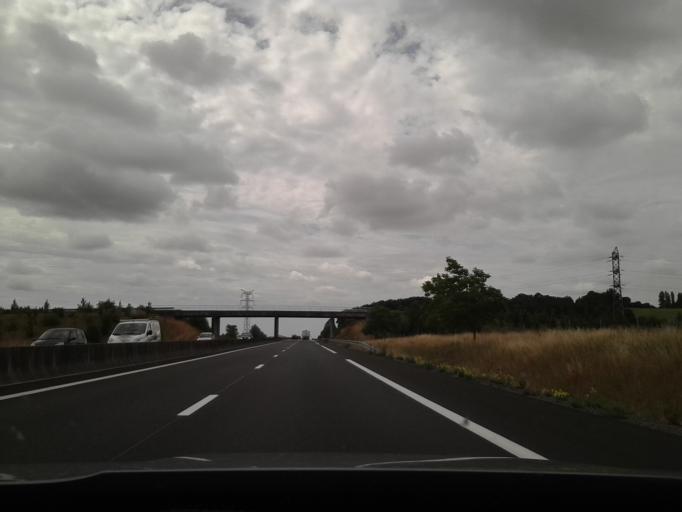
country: FR
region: Pays de la Loire
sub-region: Departement de la Sarthe
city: Arconnay
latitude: 48.3802
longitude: 0.1038
